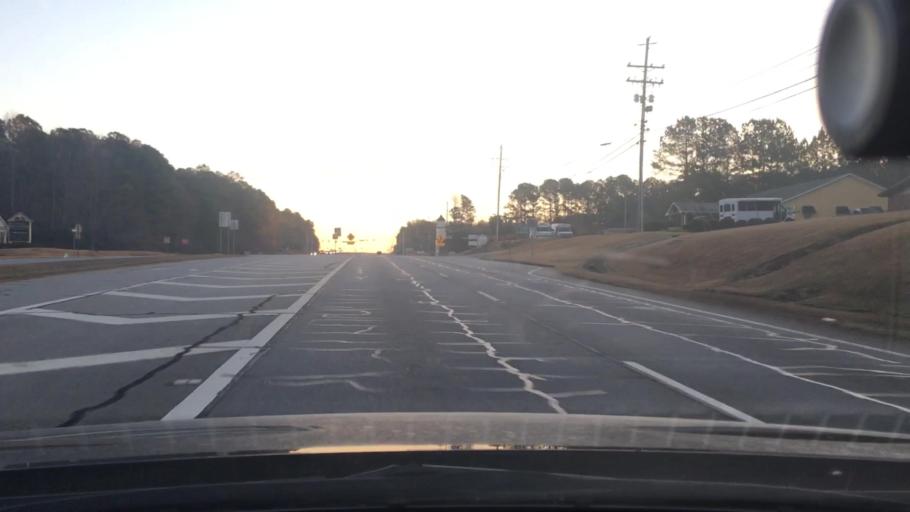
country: US
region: Georgia
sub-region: Coweta County
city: East Newnan
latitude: 33.4055
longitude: -84.7018
